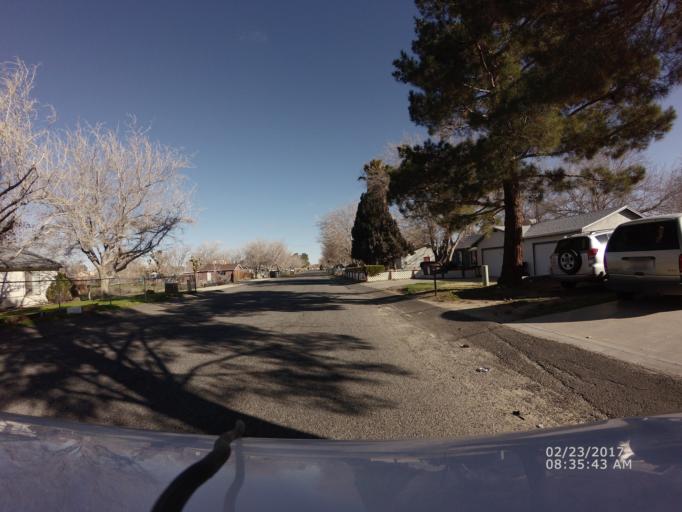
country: US
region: California
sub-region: Los Angeles County
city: Lake Los Angeles
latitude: 34.6119
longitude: -117.8332
